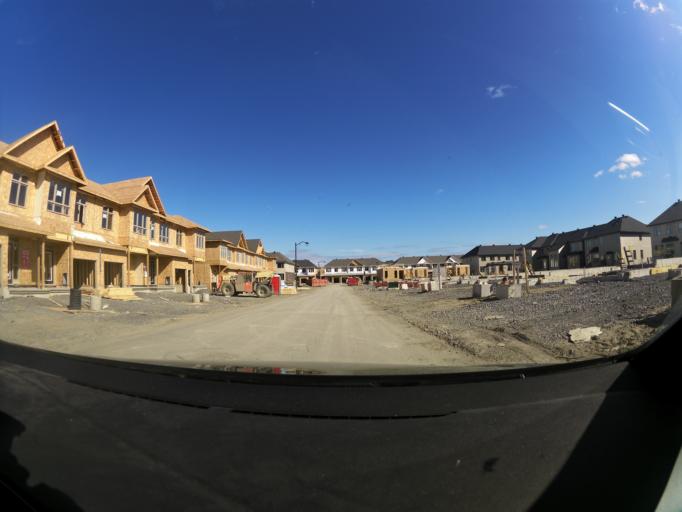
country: CA
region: Ontario
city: Bells Corners
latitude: 45.2804
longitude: -75.8946
